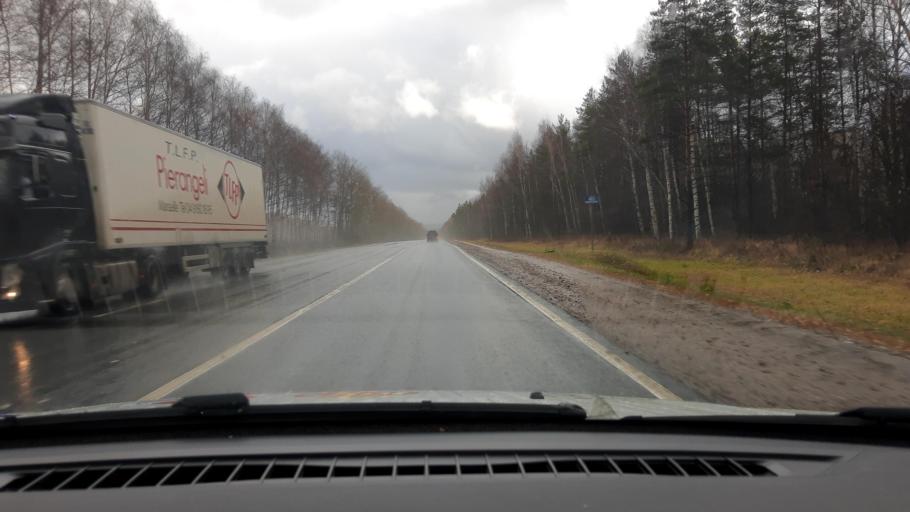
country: RU
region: Nizjnij Novgorod
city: Pamyat' Parizhskoy Kommuny
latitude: 56.0304
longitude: 44.5220
